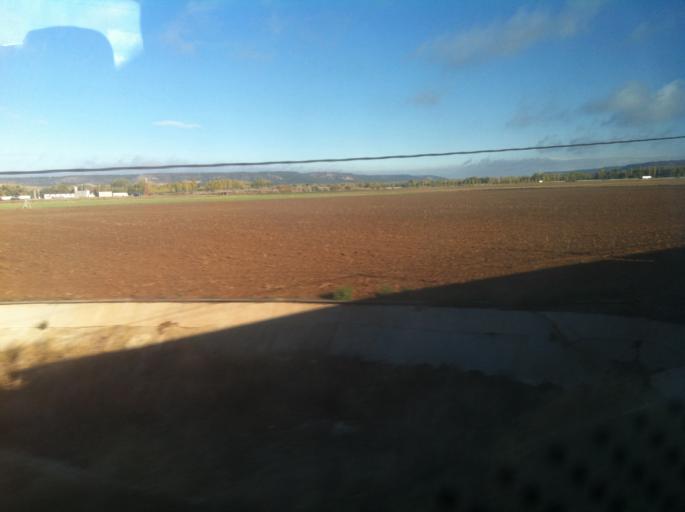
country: ES
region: Castille and Leon
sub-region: Provincia de Palencia
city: Torquemada
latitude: 42.0298
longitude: -4.2772
